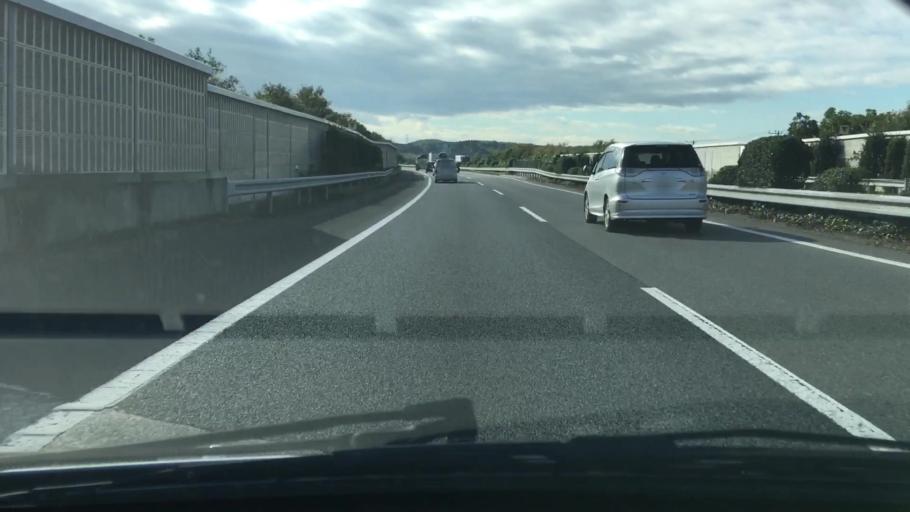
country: JP
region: Chiba
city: Ichihara
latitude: 35.4845
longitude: 140.0823
